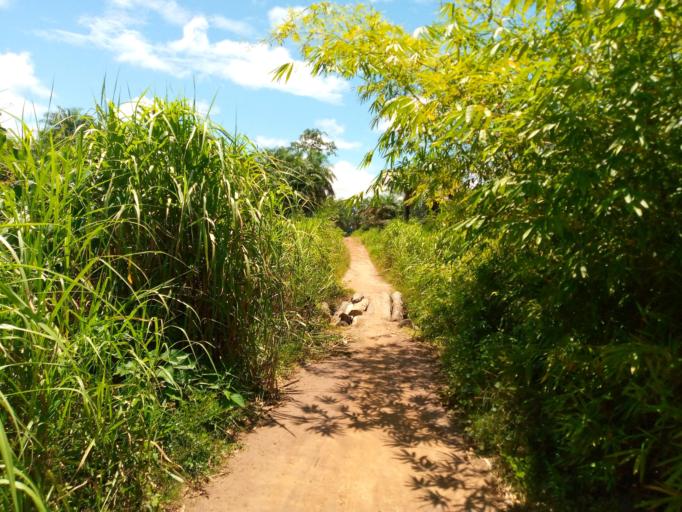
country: SL
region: Northern Province
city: Makeni
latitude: 9.0388
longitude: -12.1590
